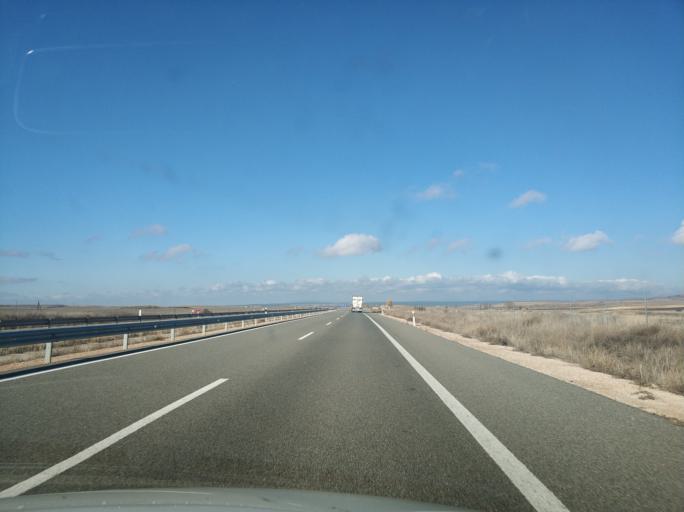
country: ES
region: Castille and Leon
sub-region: Provincia de Soria
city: Coscurita
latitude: 41.4020
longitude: -2.4782
